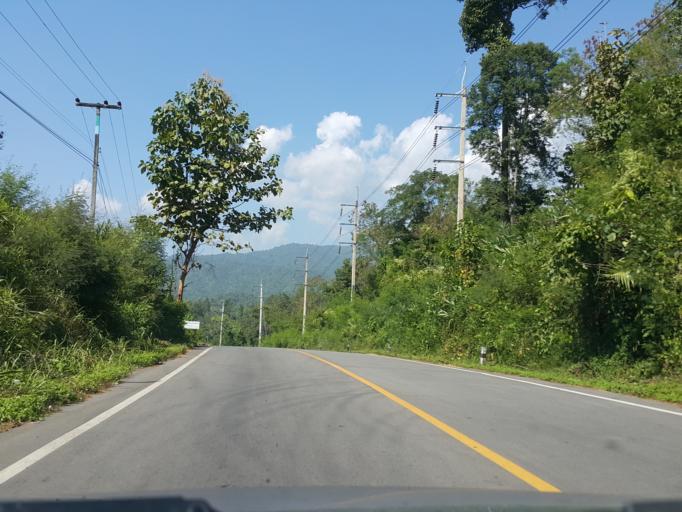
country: TH
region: Chiang Mai
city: Mae Taeng
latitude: 19.1045
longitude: 98.8150
